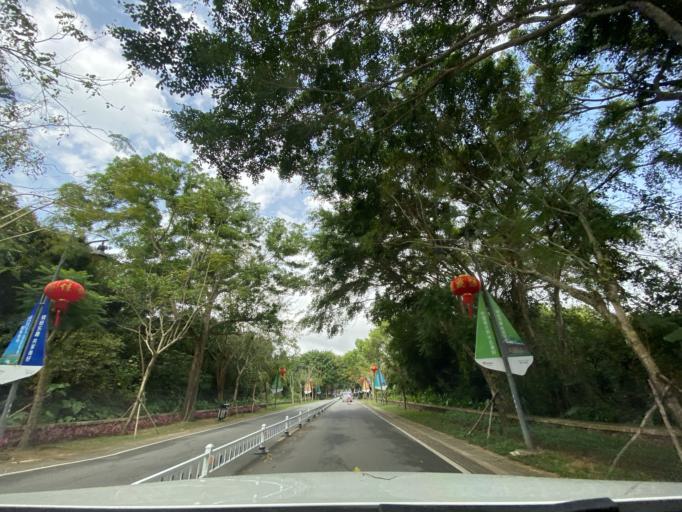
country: CN
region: Hainan
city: Liji
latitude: 18.6663
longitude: 110.2650
